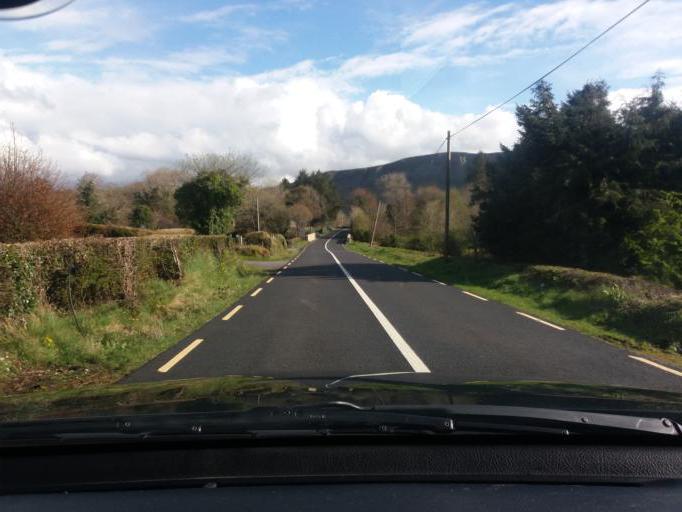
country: IE
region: Connaught
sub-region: County Leitrim
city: Kinlough
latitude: 54.3824
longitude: -8.2976
